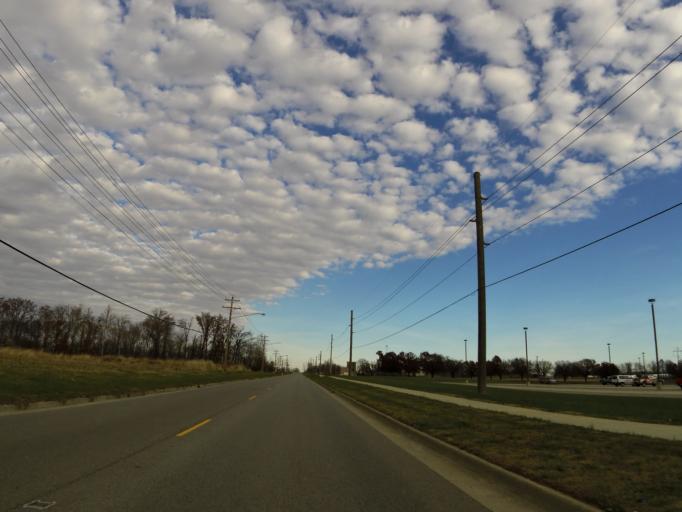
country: US
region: Illinois
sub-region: Jefferson County
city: Mount Vernon
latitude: 38.3232
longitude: -88.9700
